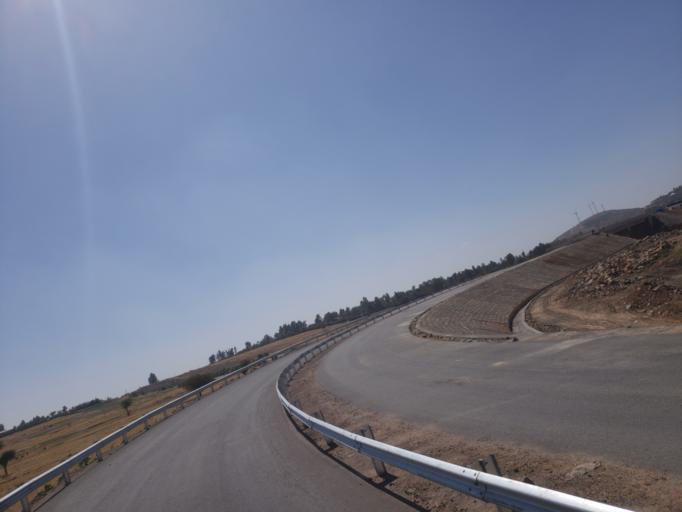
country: ET
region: Oromiya
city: Mojo
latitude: 8.5813
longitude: 39.1737
